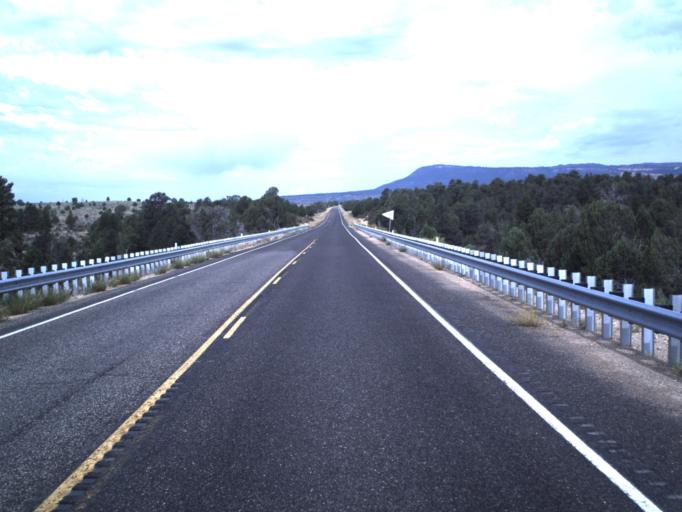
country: US
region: Utah
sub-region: Kane County
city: Kanab
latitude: 37.2215
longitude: -112.7126
